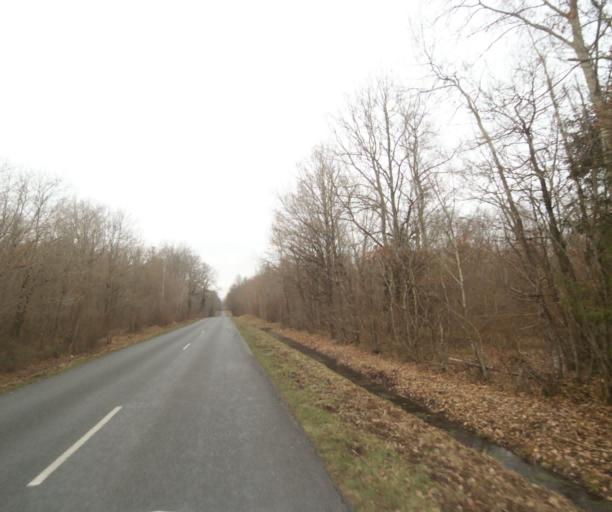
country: FR
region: Champagne-Ardenne
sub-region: Departement de la Marne
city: Pargny-sur-Saulx
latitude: 48.7242
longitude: 4.8723
